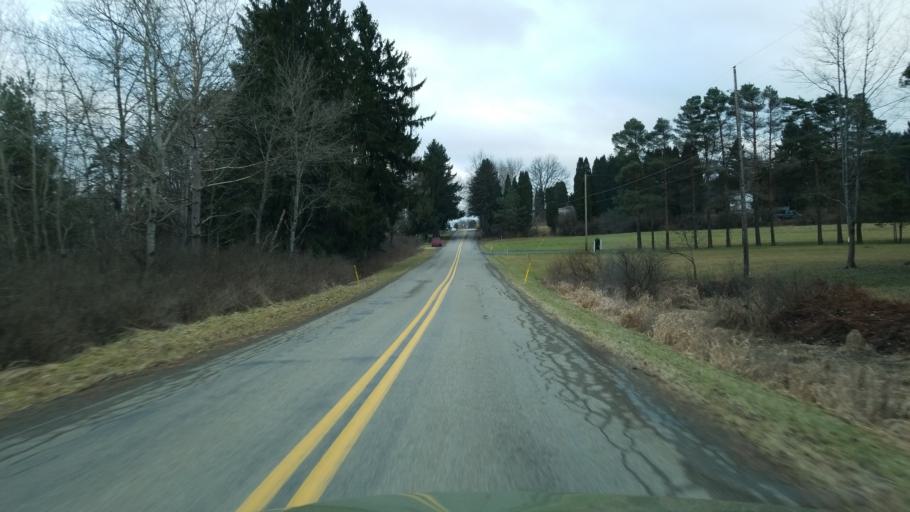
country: US
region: Pennsylvania
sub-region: Jefferson County
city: Falls Creek
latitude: 41.1693
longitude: -78.8118
